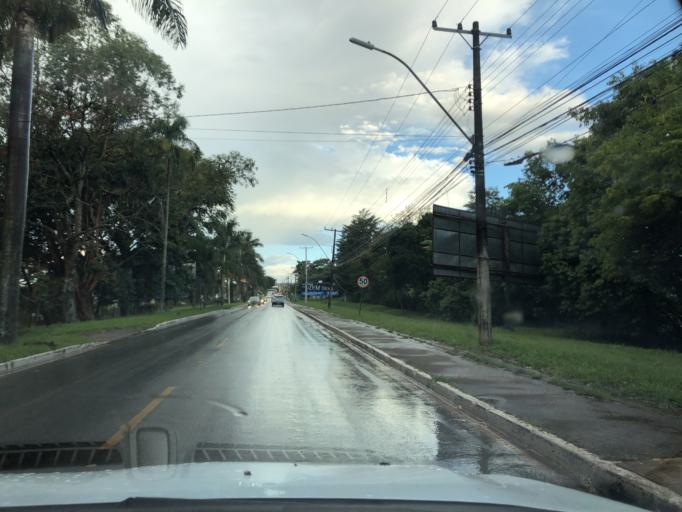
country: BR
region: Federal District
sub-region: Brasilia
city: Brasilia
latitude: -15.8760
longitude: -47.9643
